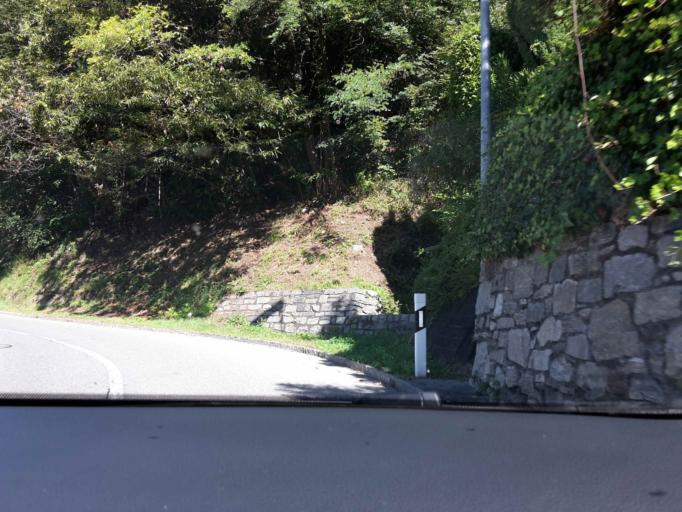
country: CH
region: Ticino
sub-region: Bellinzona District
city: Giubiasco
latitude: 46.1709
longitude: 9.0309
